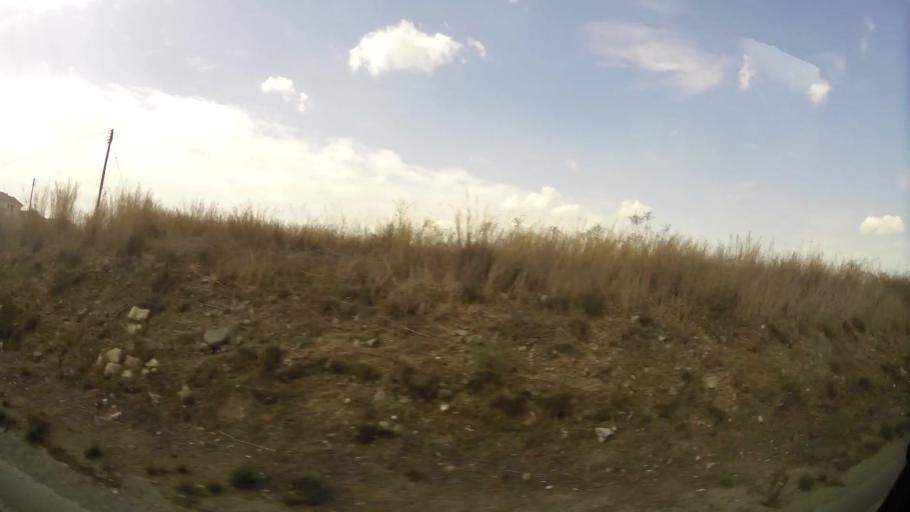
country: CY
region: Lefkosia
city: Tseri
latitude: 35.1001
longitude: 33.3275
